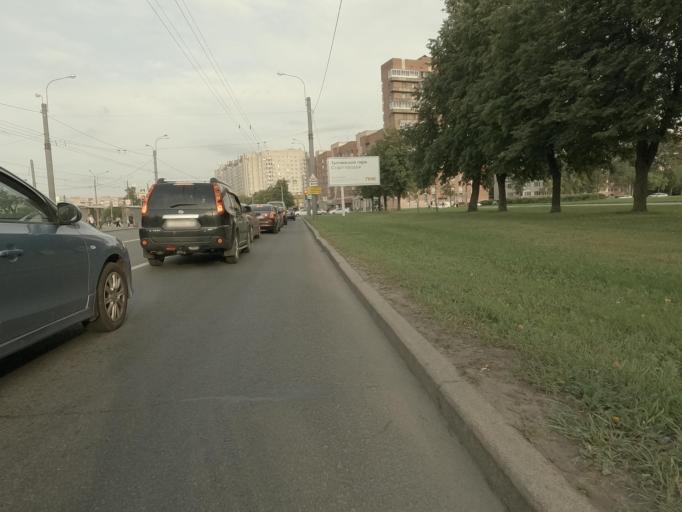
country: RU
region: St.-Petersburg
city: Uritsk
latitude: 59.8334
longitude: 30.1637
